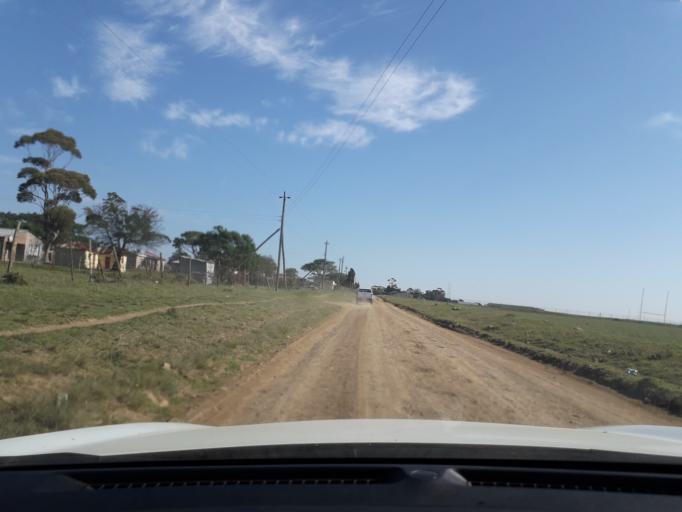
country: ZA
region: Eastern Cape
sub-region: Buffalo City Metropolitan Municipality
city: Bhisho
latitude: -32.9716
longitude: 27.3114
